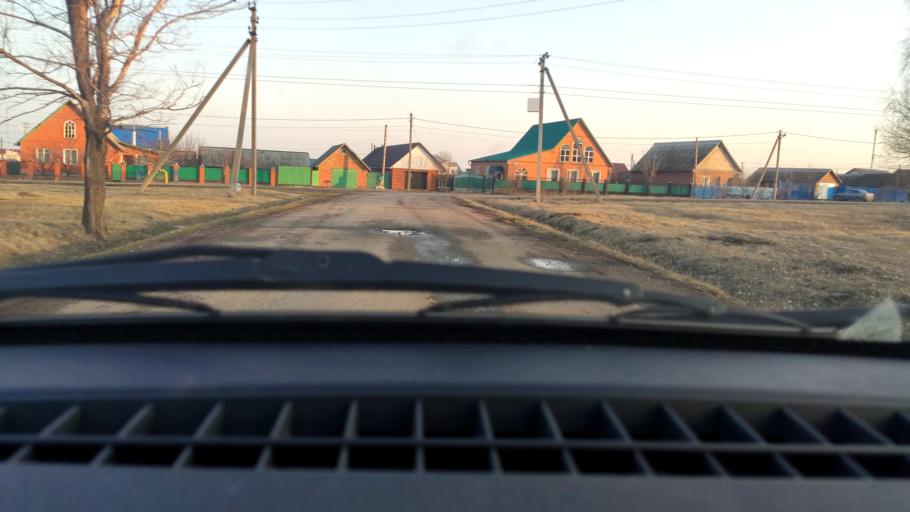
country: RU
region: Bashkortostan
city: Davlekanovo
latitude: 54.2347
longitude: 55.0287
